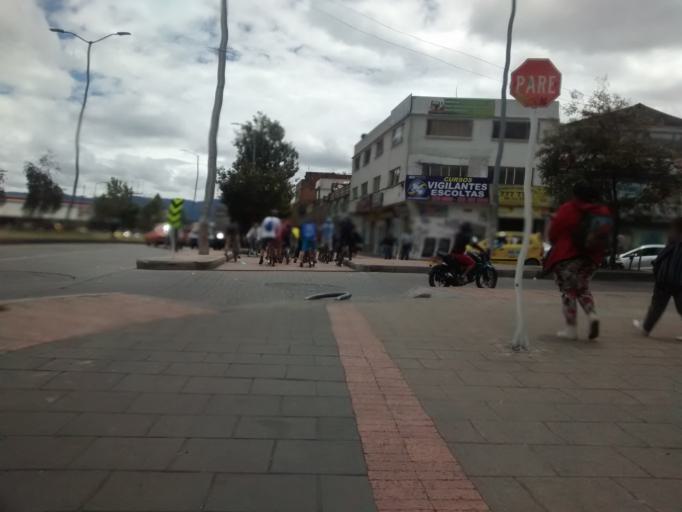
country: CO
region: Bogota D.C.
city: Bogota
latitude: 4.5953
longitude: -74.1414
